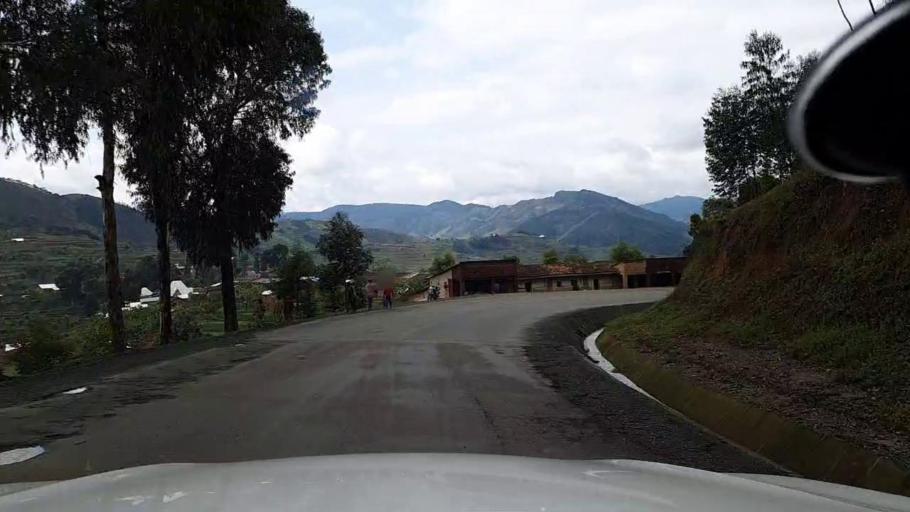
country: RW
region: Western Province
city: Kibuye
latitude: -2.0655
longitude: 29.5397
